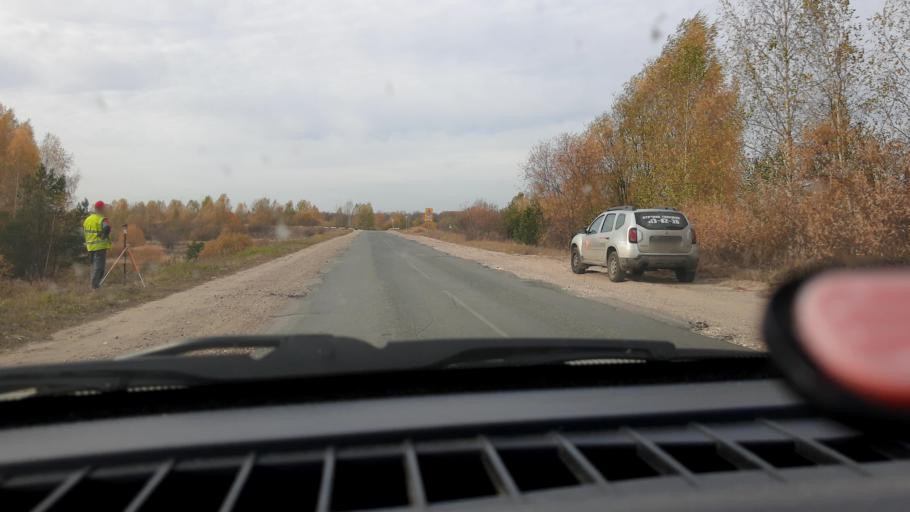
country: RU
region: Nizjnij Novgorod
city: Neklyudovo
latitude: 56.4217
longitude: 43.9298
